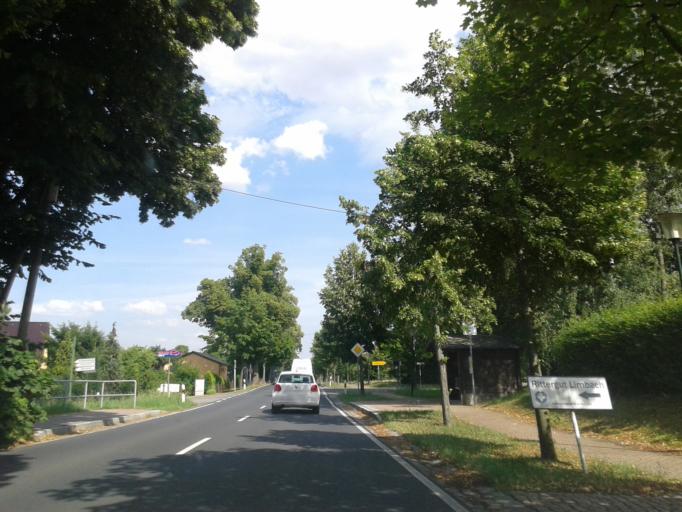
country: DE
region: Saxony
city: Wilsdruff
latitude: 51.0508
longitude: 13.4787
